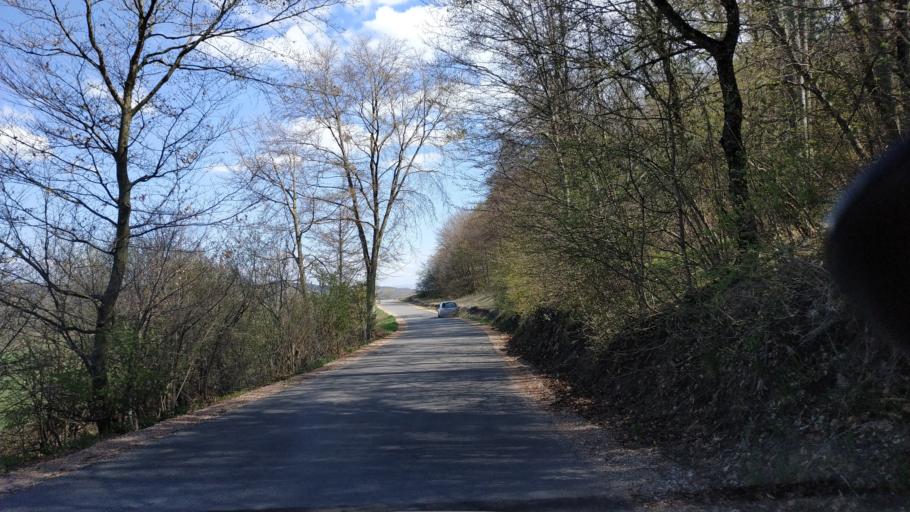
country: RS
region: Central Serbia
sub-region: Zajecarski Okrug
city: Soko Banja
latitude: 43.5840
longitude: 21.8903
